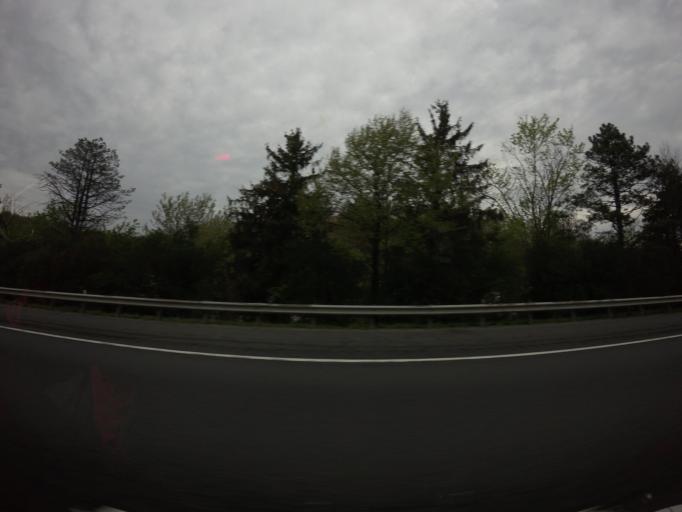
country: US
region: Maryland
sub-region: Carroll County
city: Mount Airy
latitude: 39.3651
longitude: -77.1840
